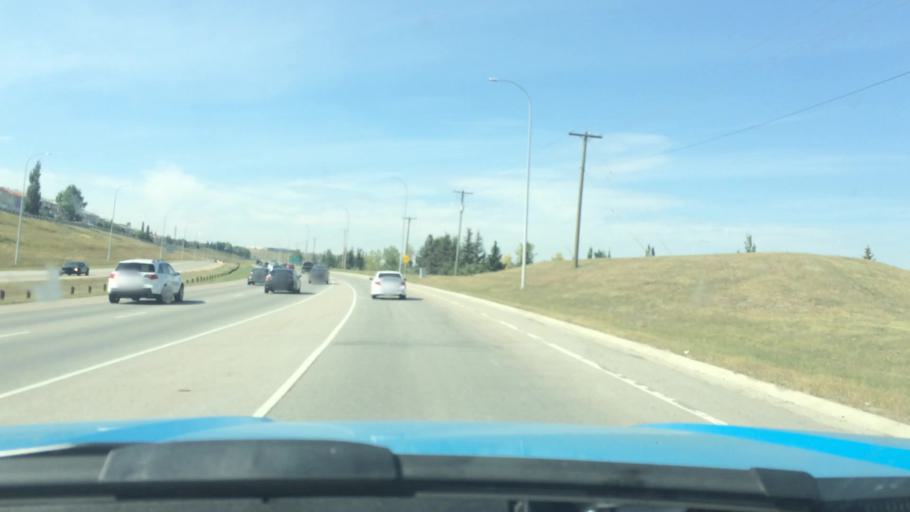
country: CA
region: Alberta
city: Calgary
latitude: 51.1444
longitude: -114.1250
